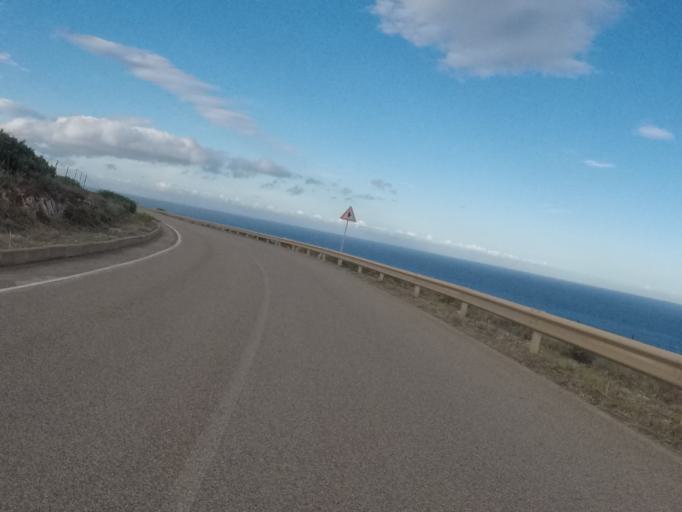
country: IT
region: Sardinia
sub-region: Provincia di Carbonia-Iglesias
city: Buggerru
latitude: 39.3957
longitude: 8.3964
